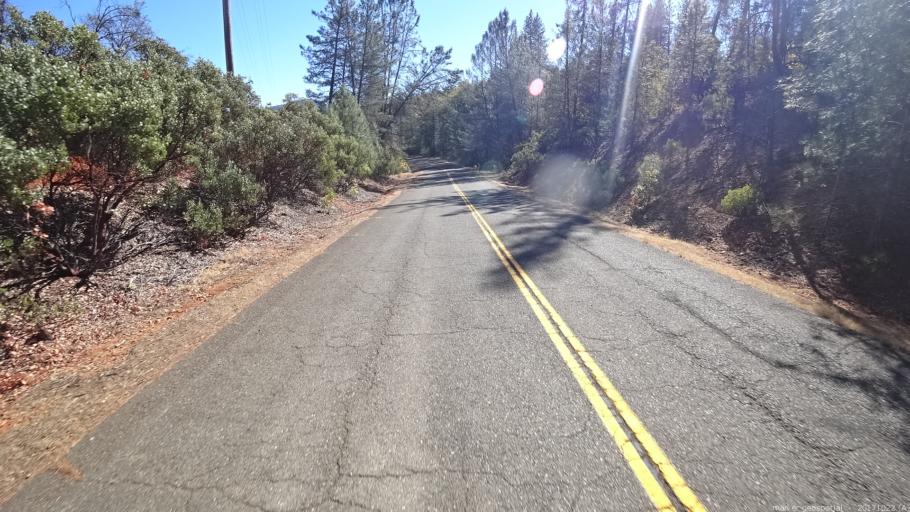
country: US
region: California
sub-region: Shasta County
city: Central Valley (historical)
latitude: 40.9187
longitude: -122.4018
